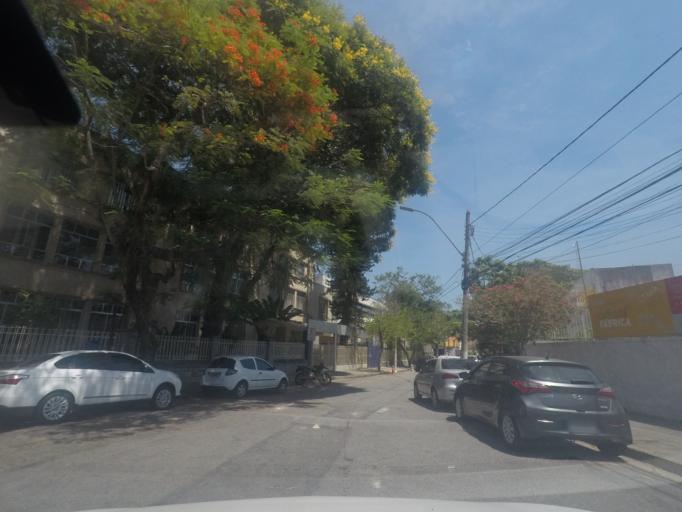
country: BR
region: Rio de Janeiro
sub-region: Niteroi
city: Niteroi
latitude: -22.9212
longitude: -43.0923
